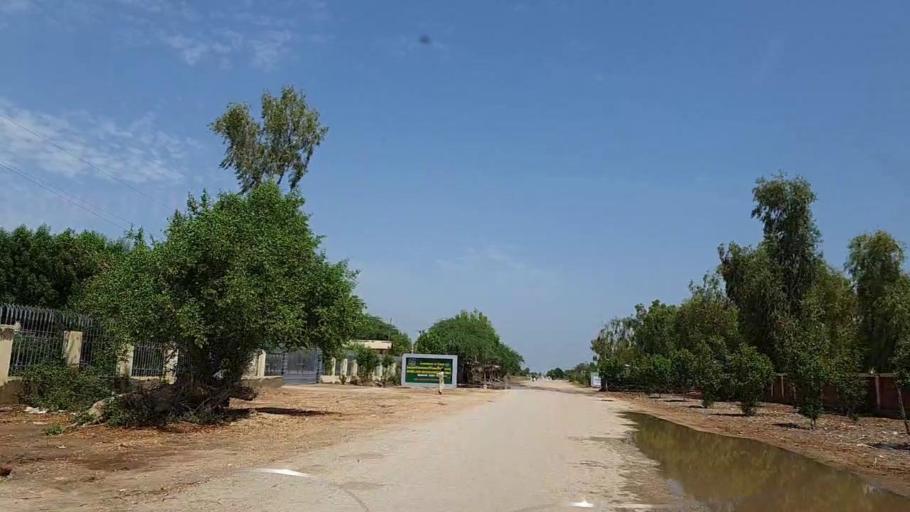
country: PK
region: Sindh
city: Naushahro Firoz
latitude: 26.8299
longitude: 68.1419
